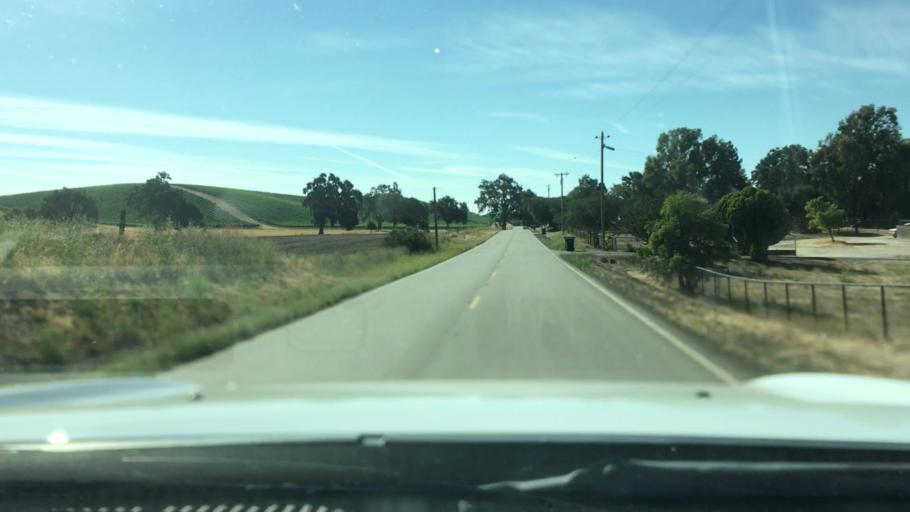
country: US
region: California
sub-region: San Luis Obispo County
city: Templeton
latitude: 35.5604
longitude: -120.6354
